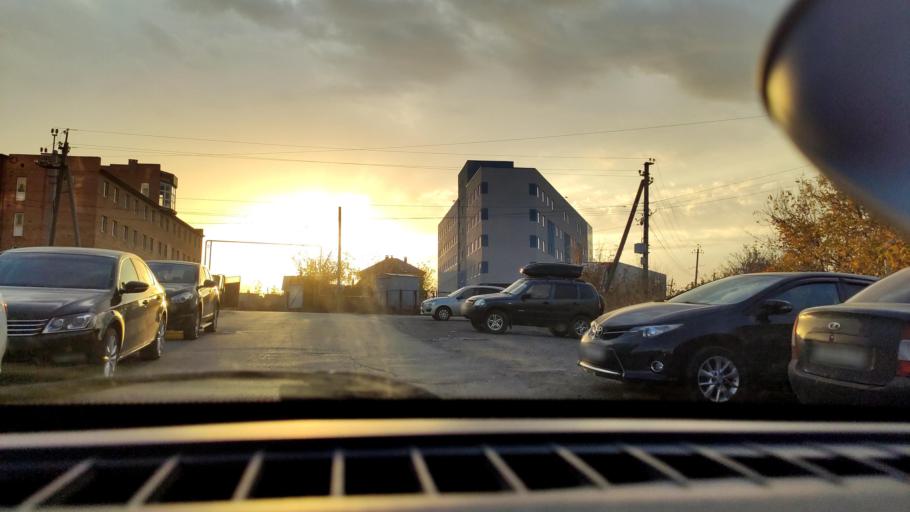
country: RU
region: Samara
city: Samara
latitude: 53.2742
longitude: 50.2267
